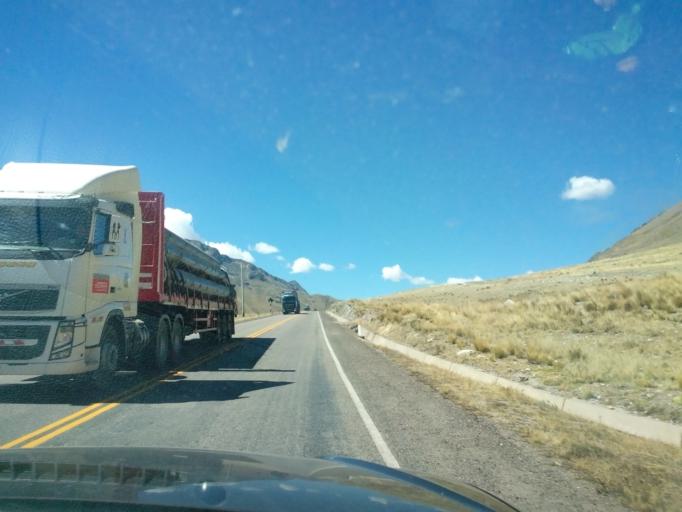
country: PE
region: Cusco
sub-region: Provincia de Canas
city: Layo
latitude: -14.4813
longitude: -71.0007
